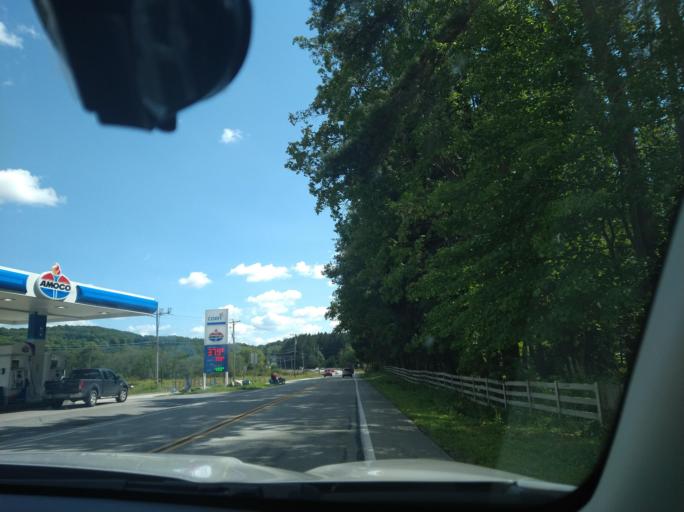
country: US
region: Pennsylvania
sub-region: Somerset County
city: Milford
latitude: 40.0352
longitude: -79.2140
